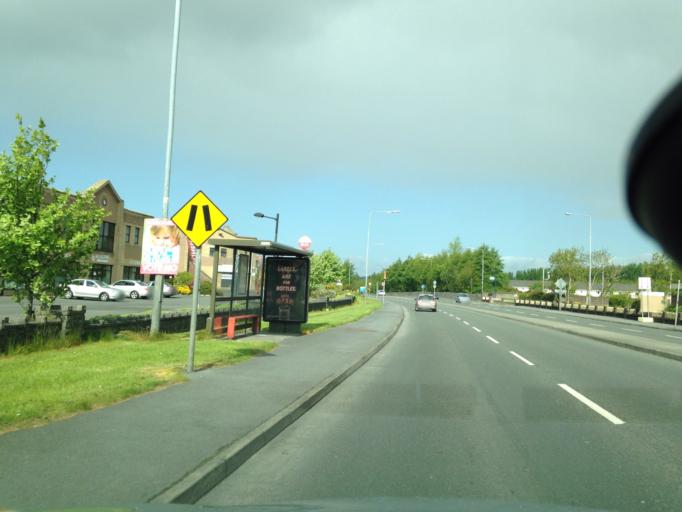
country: IE
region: Connaught
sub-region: County Galway
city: Gaillimh
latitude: 53.2826
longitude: -9.0398
